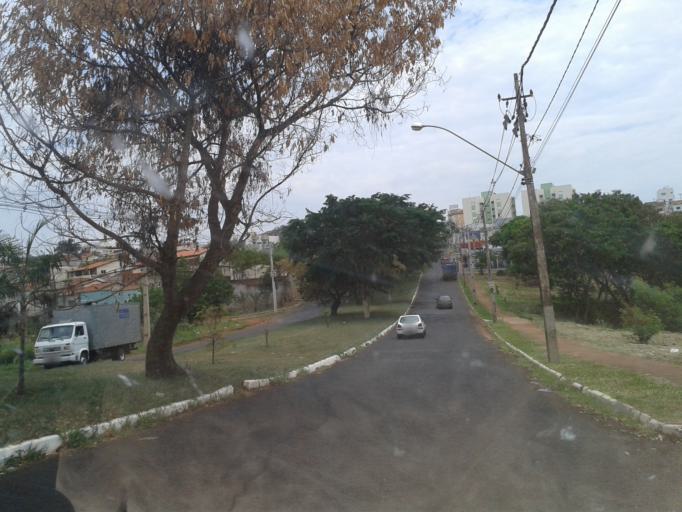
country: BR
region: Minas Gerais
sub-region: Uberlandia
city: Uberlandia
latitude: -18.9165
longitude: -48.3123
